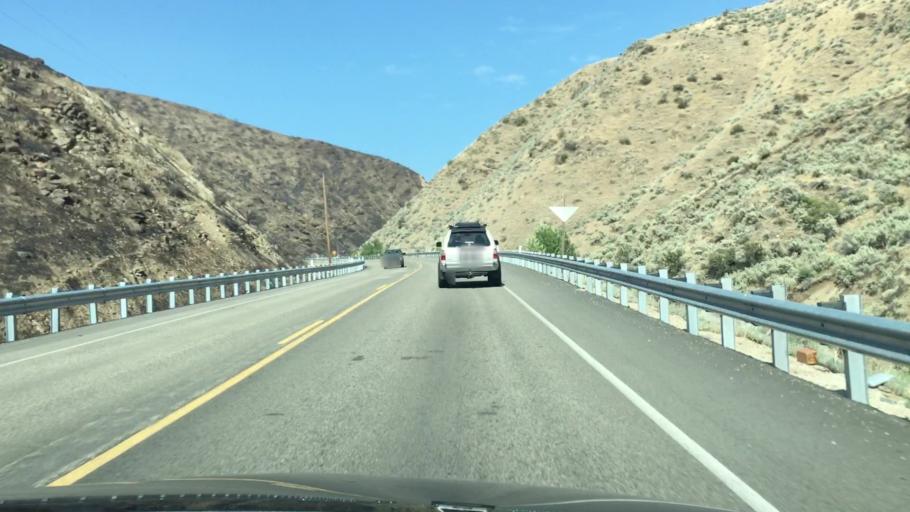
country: US
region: Idaho
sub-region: Ada County
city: Eagle
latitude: 43.7582
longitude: -116.2758
